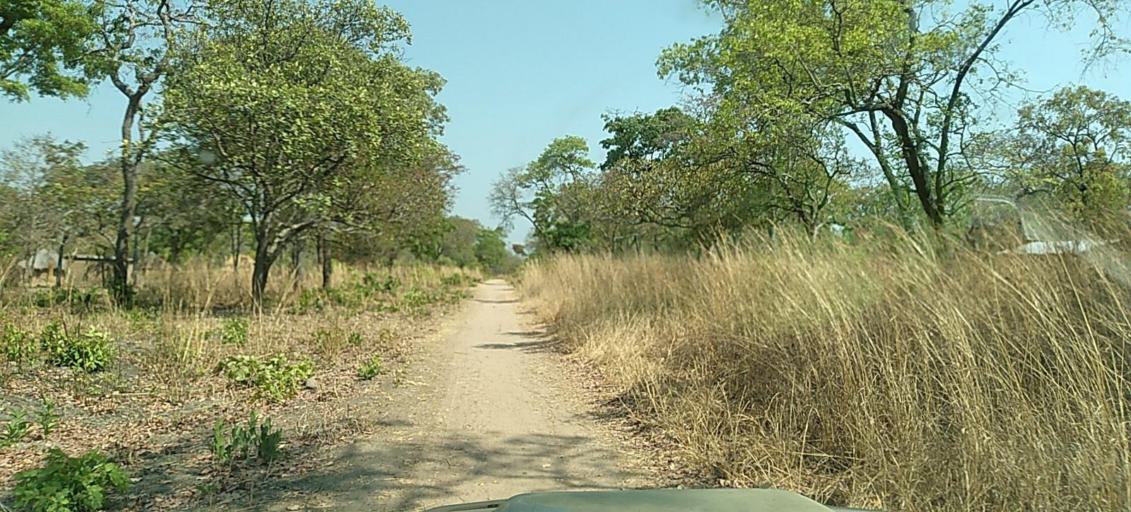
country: ZM
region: North-Western
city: Kalengwa
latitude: -13.3049
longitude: 24.8010
